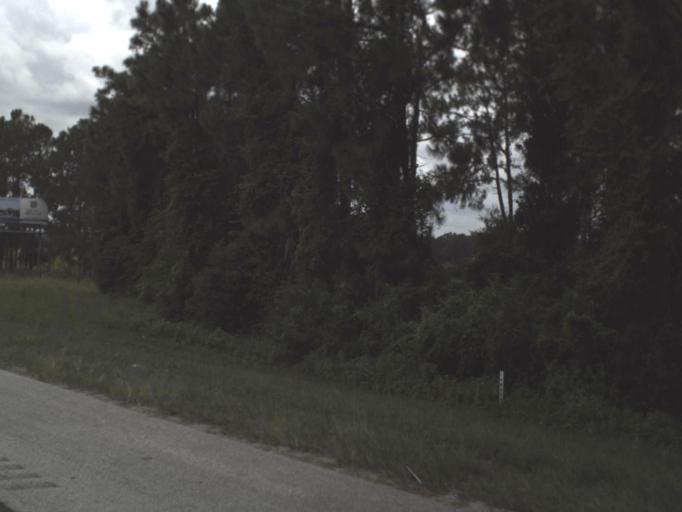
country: US
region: Florida
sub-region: Pasco County
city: San Antonio
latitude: 28.3932
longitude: -82.3195
